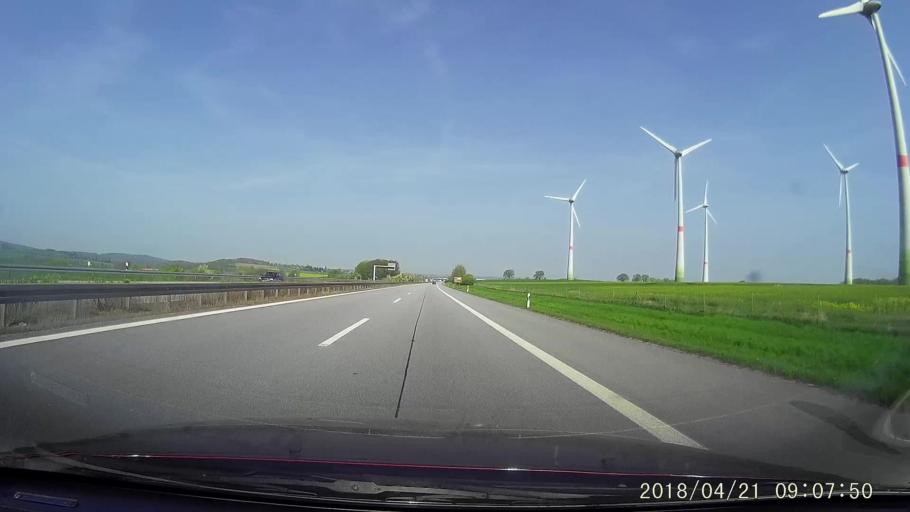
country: DE
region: Saxony
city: Goerlitz
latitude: 51.2040
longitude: 14.9507
